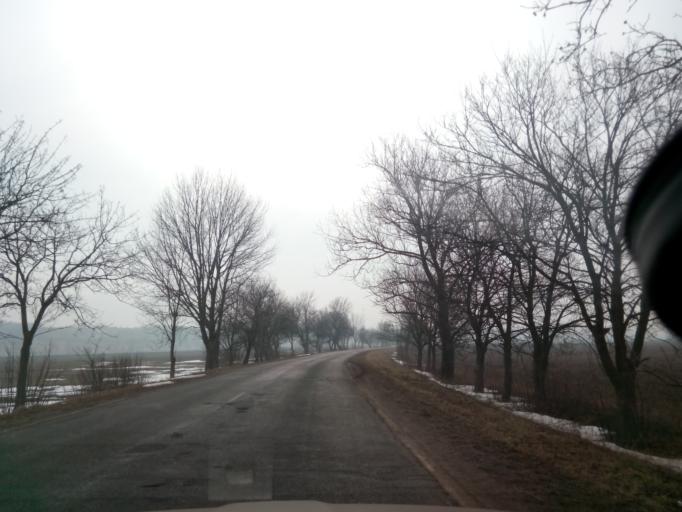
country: HU
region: Borsod-Abauj-Zemplen
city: Gonc
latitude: 48.4899
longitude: 21.2509
